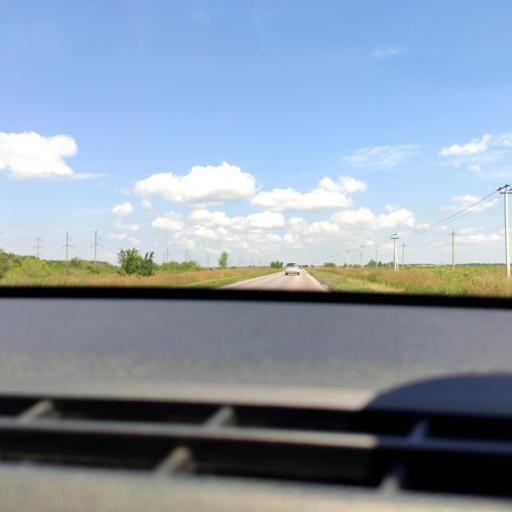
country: RU
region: Samara
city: Podstepki
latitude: 53.5430
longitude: 49.0880
